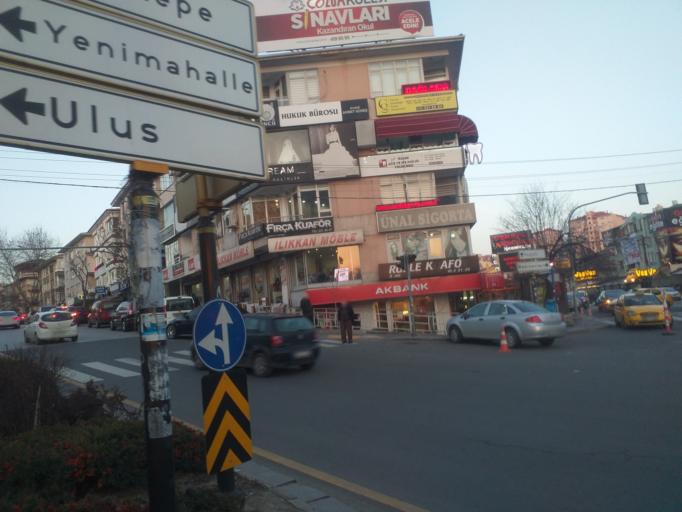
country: TR
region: Ankara
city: Ankara
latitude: 39.9731
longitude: 32.8426
